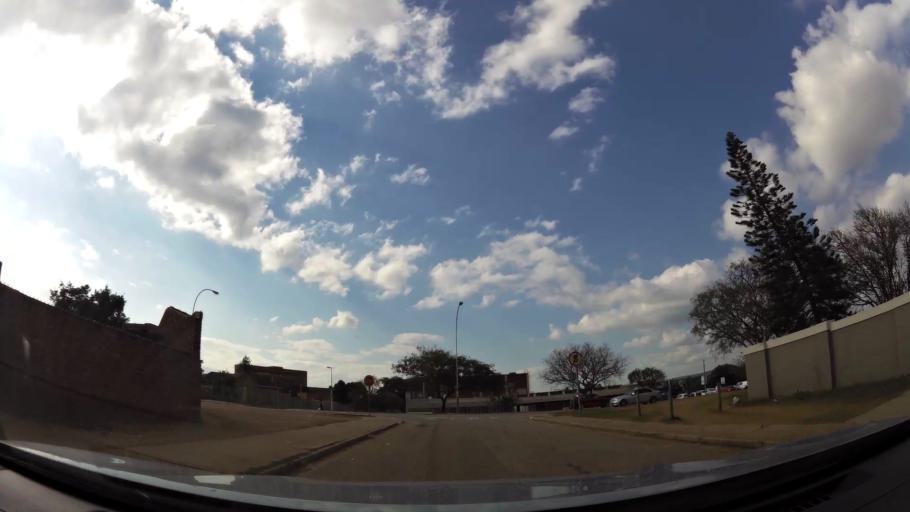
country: ZA
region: Eastern Cape
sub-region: Nelson Mandela Bay Metropolitan Municipality
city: Uitenhage
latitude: -33.7436
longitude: 25.4075
